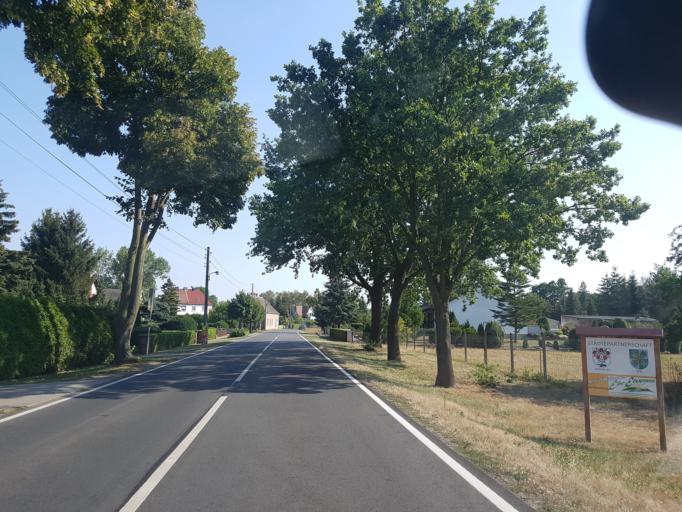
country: DE
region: Saxony-Anhalt
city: Annaburg
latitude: 51.7392
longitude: 13.0414
